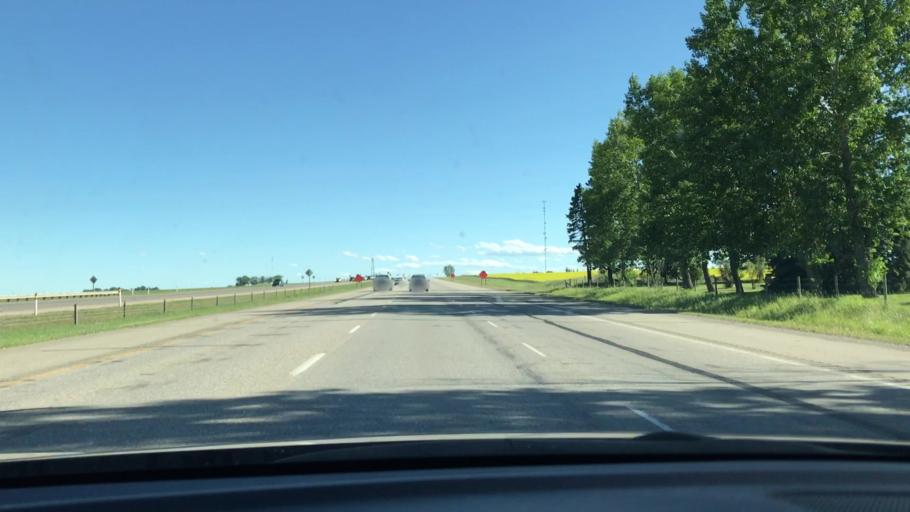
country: CA
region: Alberta
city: Crossfield
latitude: 51.4308
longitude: -114.0020
